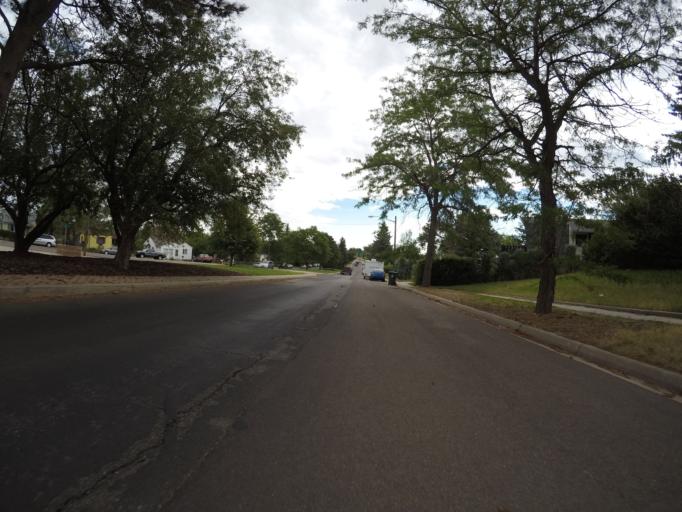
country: US
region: Wyoming
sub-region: Laramie County
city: Cheyenne
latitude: 41.1439
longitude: -104.7941
